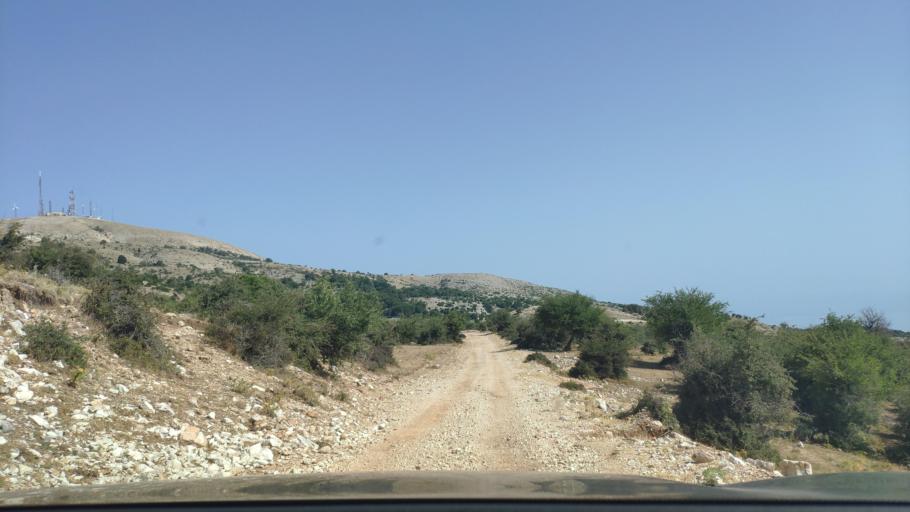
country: GR
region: West Greece
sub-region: Nomos Aitolias kai Akarnanias
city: Monastirakion
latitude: 38.7977
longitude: 20.9980
